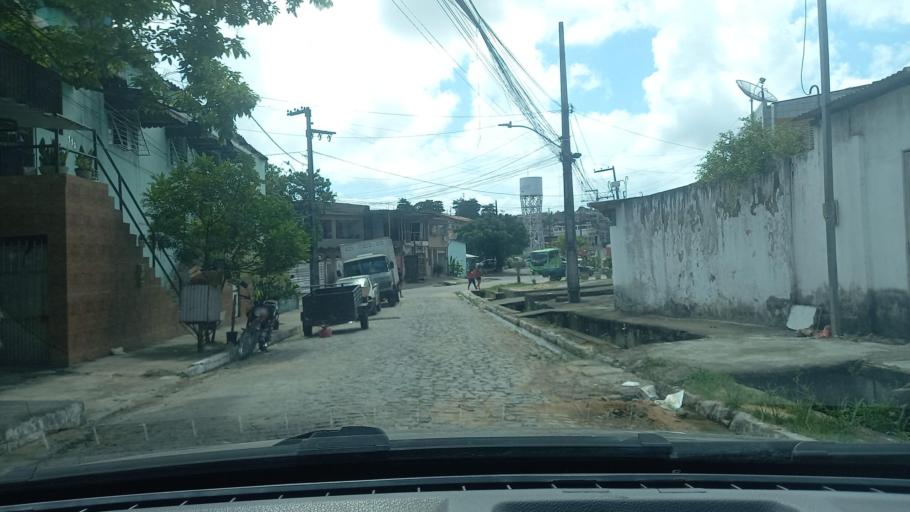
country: BR
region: Pernambuco
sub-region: Jaboatao Dos Guararapes
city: Jaboatao dos Guararapes
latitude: -8.1275
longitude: -34.9515
